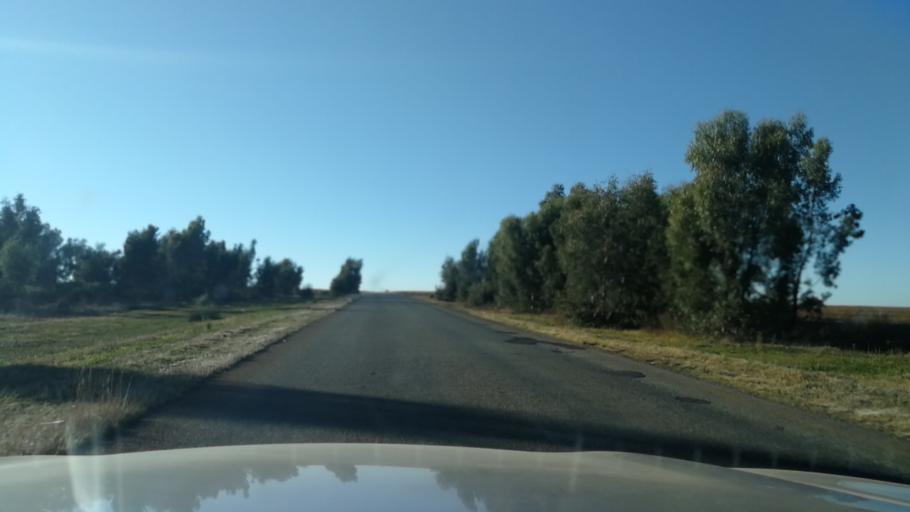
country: ZA
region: North-West
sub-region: Bojanala Platinum District Municipality
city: Rustenburg
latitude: -25.9807
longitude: 27.2616
